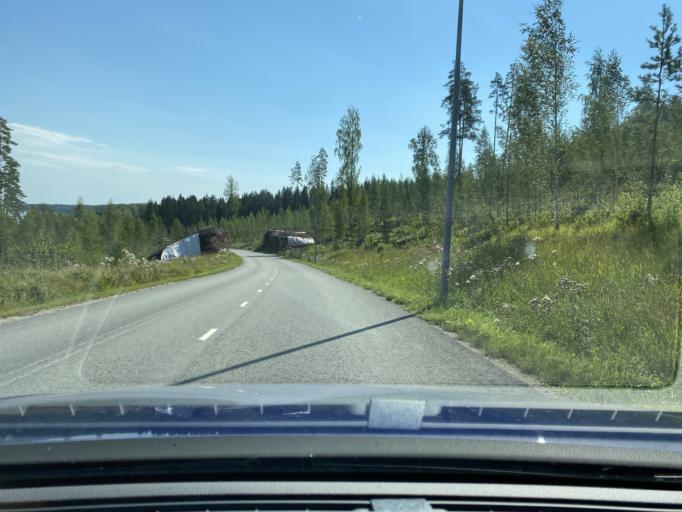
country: FI
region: Central Finland
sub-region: Jaemsae
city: Jaemsae
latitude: 61.8899
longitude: 25.3904
